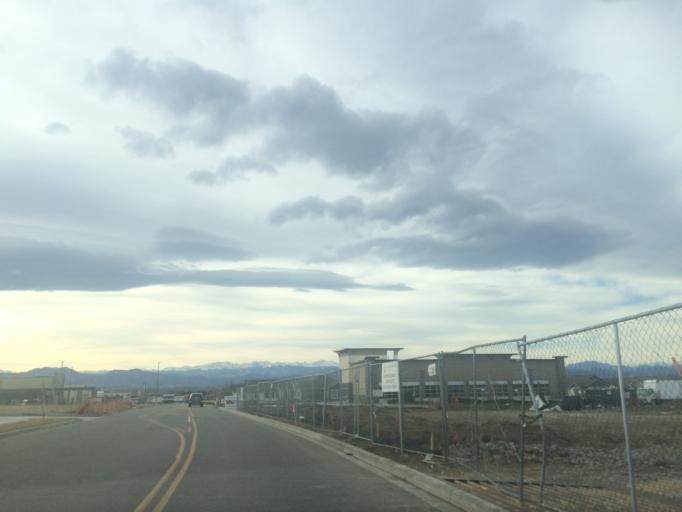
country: US
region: Colorado
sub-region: Boulder County
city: Erie
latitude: 40.0011
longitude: -105.0123
